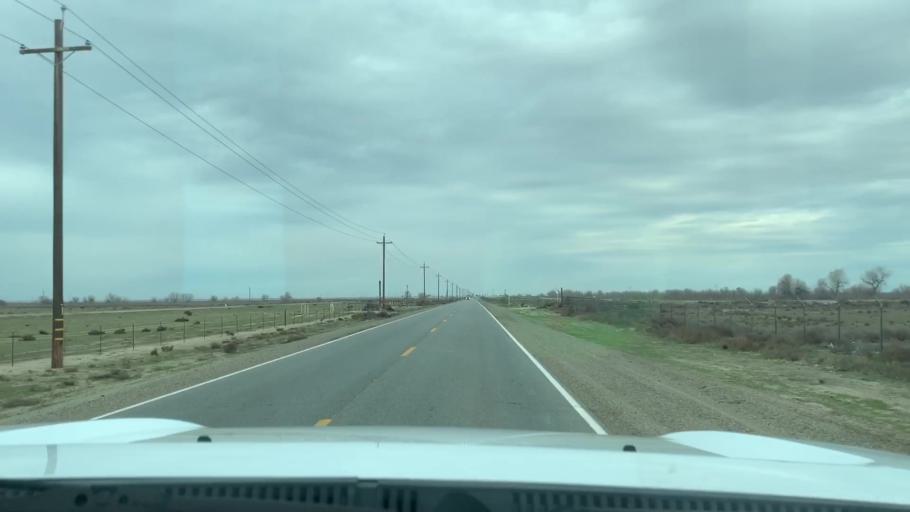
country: US
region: California
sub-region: Kern County
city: Rosedale
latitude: 35.3279
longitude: -119.2524
